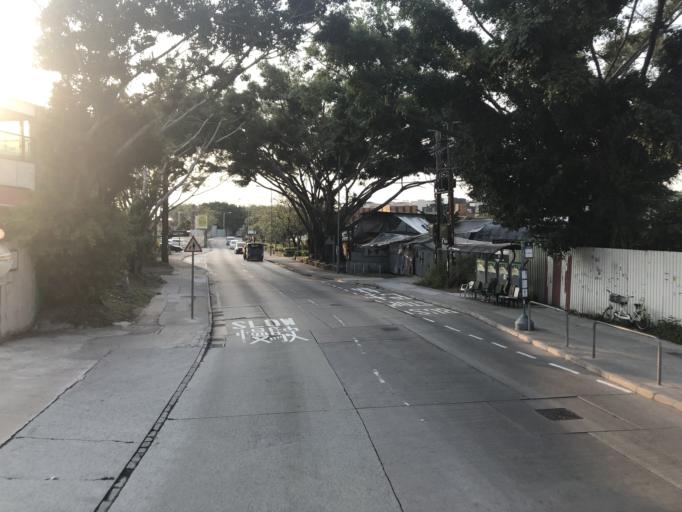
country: HK
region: Yuen Long
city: Yuen Long Kau Hui
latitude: 22.4611
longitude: 113.9895
